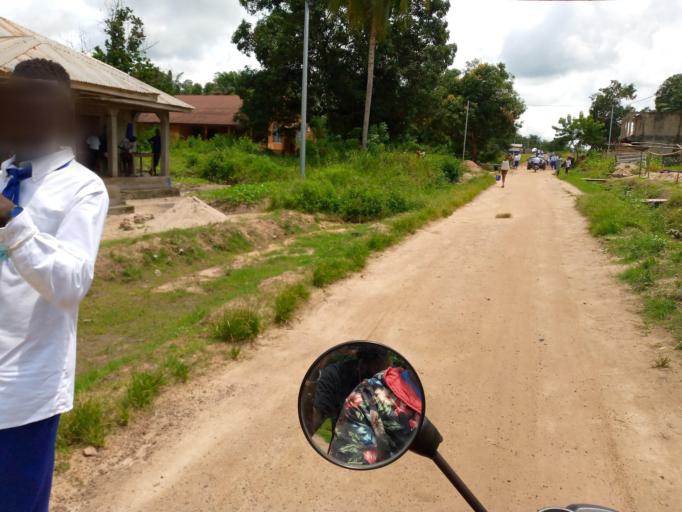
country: SL
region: Northern Province
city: Binkolo
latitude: 9.1096
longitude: -12.2036
